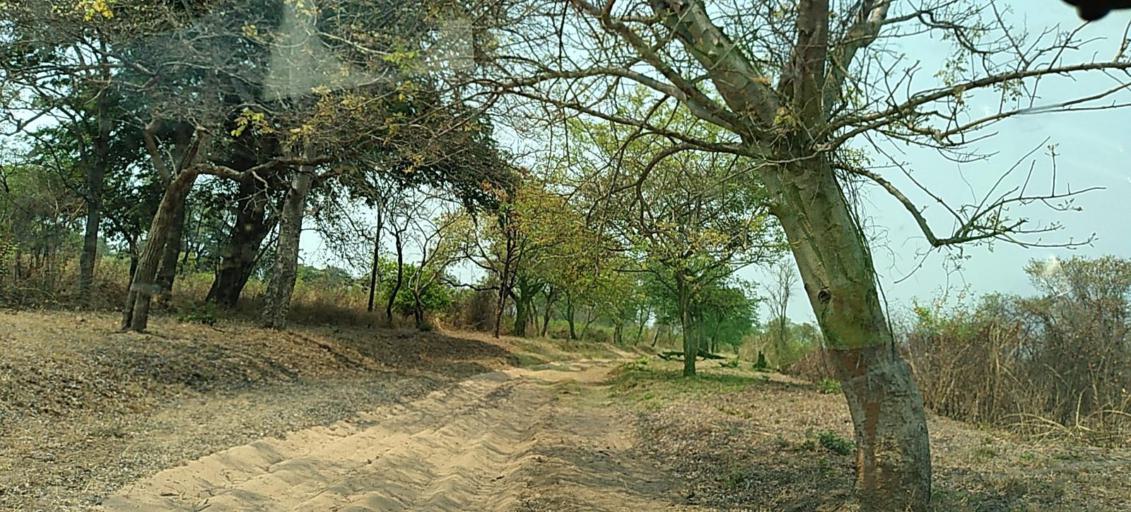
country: ZM
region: Western
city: Lukulu
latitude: -13.9702
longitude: 23.2301
